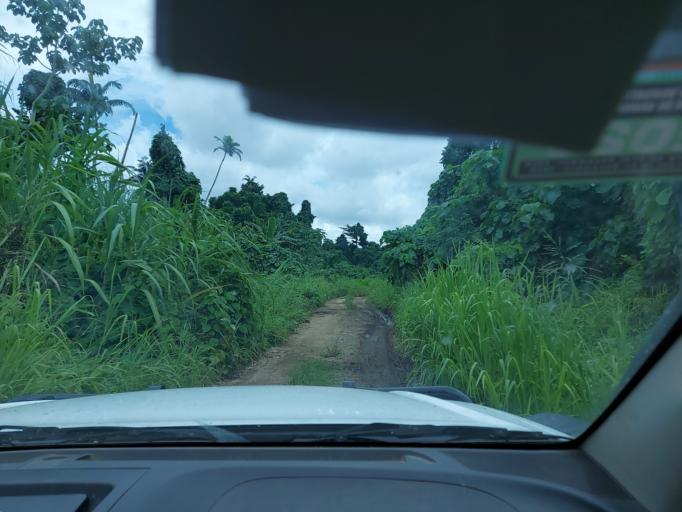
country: VU
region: Malampa
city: Lakatoro
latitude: -16.2744
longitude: 167.6301
